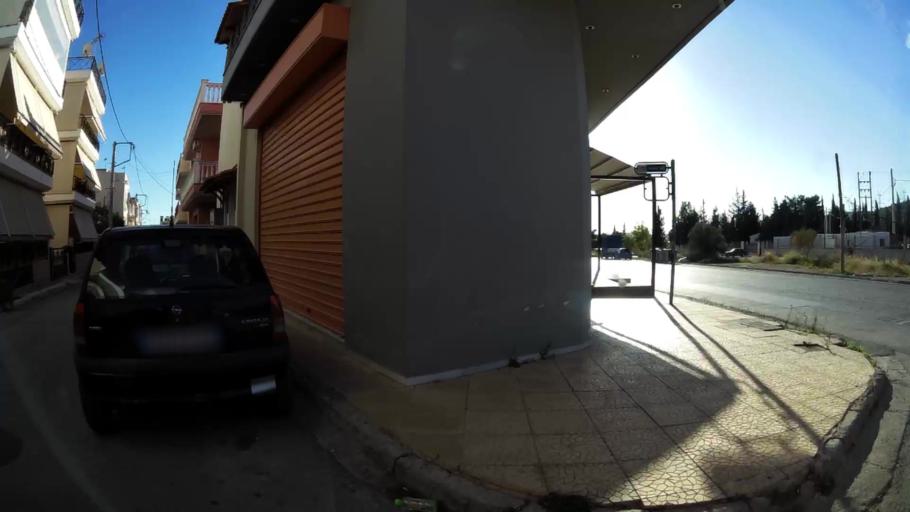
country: GR
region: Attica
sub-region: Nomarchia Anatolikis Attikis
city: Acharnes
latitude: 38.0935
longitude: 23.7236
